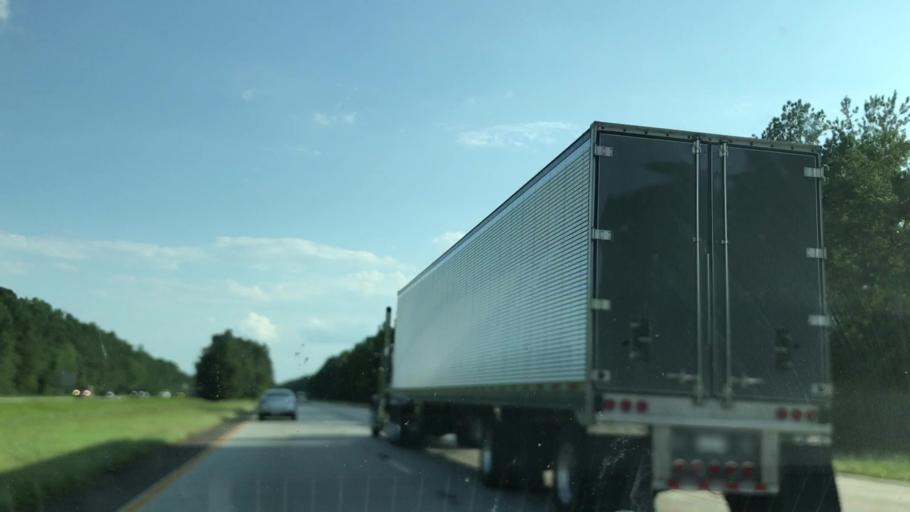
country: US
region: South Carolina
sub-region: Dorchester County
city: Saint George
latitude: 33.0804
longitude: -80.6550
